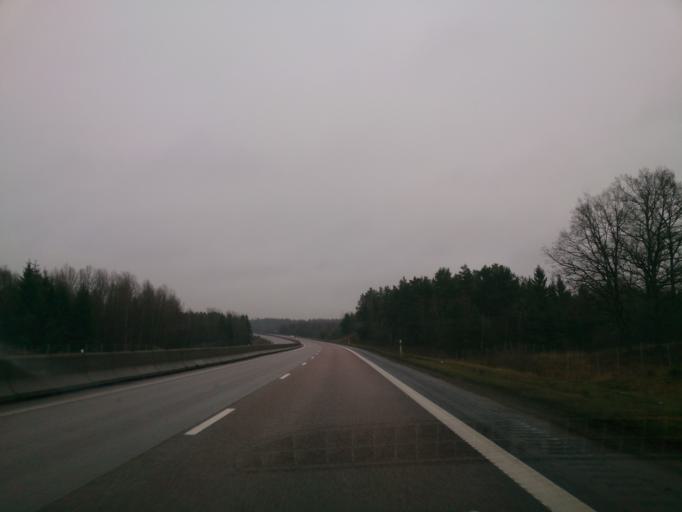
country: SE
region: OEstergoetland
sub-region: Norrkopings Kommun
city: Kimstad
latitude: 58.5035
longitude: 15.9871
